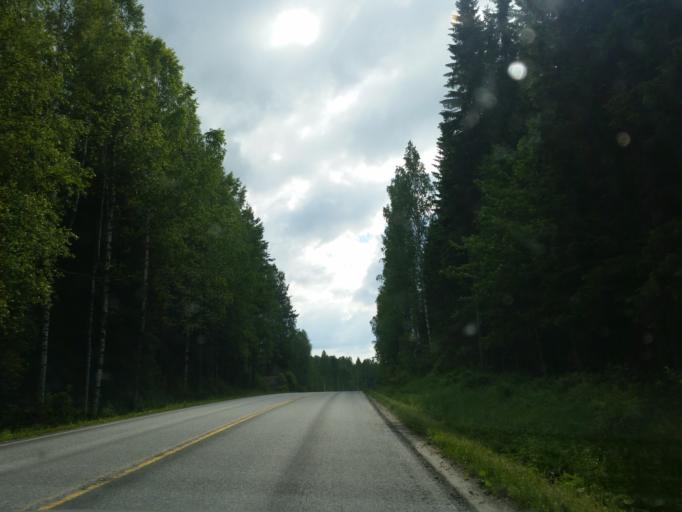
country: FI
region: Northern Savo
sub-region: Kuopio
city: Kuopio
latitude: 62.8458
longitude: 27.4584
